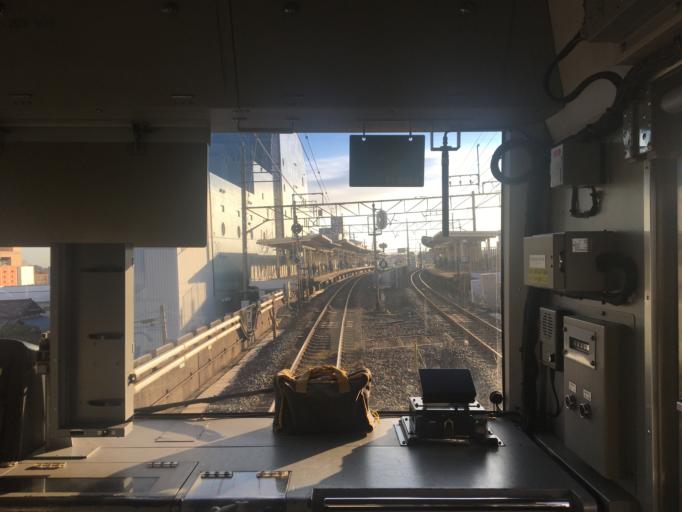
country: JP
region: Saitama
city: Yoshikawa
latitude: 35.8767
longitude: 139.8419
